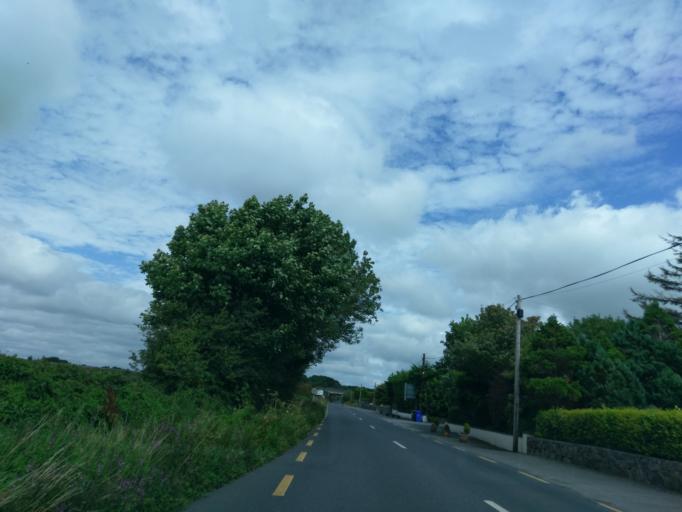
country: IE
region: Connaught
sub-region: County Galway
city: Oranmore
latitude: 53.2765
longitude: -8.8533
